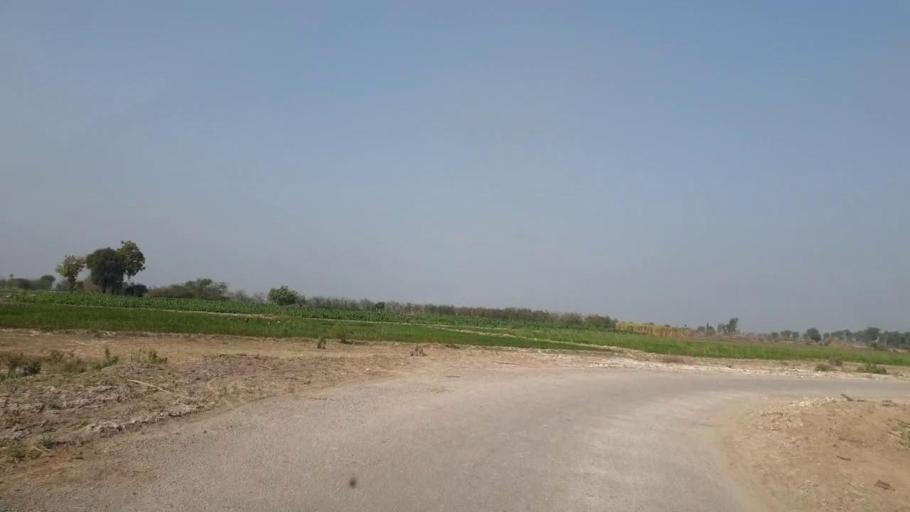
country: PK
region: Sindh
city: Mirpur Khas
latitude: 25.5820
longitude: 69.0054
